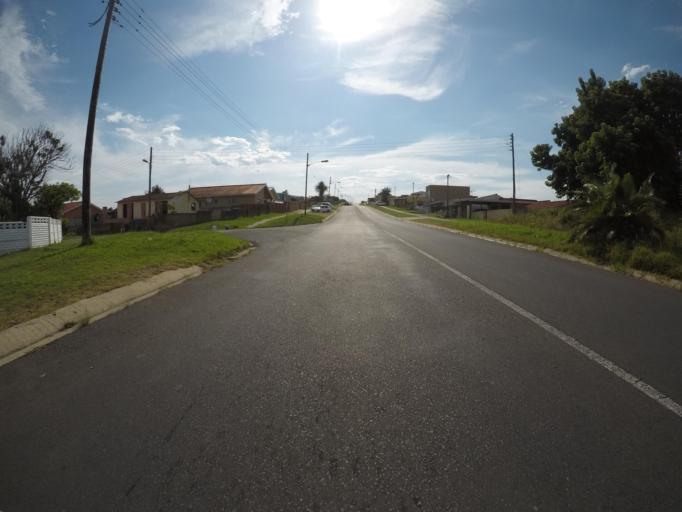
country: ZA
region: Eastern Cape
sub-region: Buffalo City Metropolitan Municipality
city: East London
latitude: -33.0228
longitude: 27.8773
